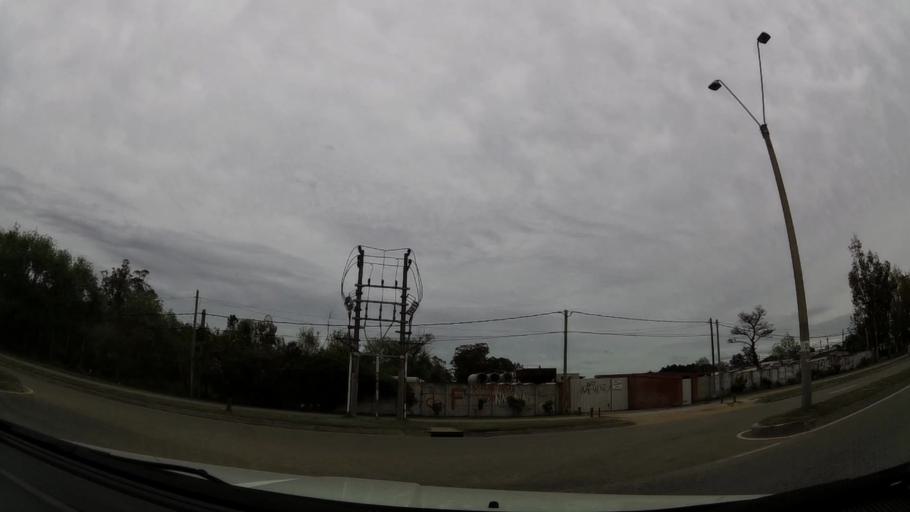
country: UY
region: Maldonado
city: Maldonado
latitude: -34.8874
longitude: -54.9660
